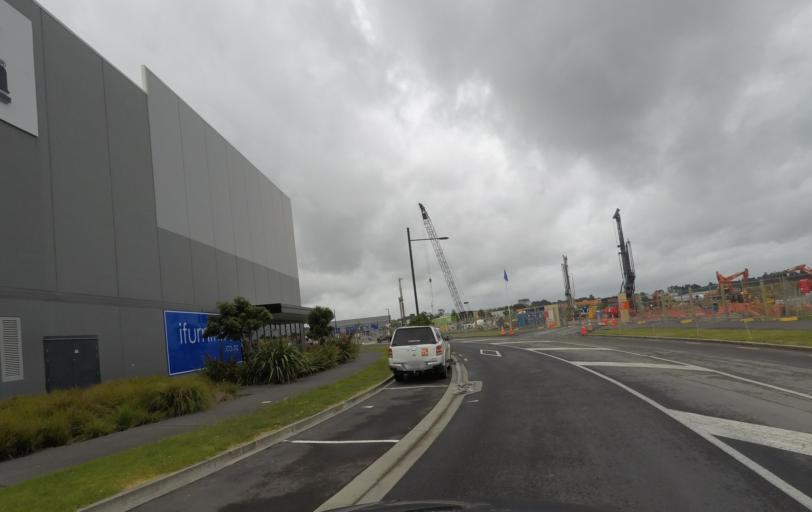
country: NZ
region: Auckland
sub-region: Auckland
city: Rosebank
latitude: -36.8117
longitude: 174.6096
